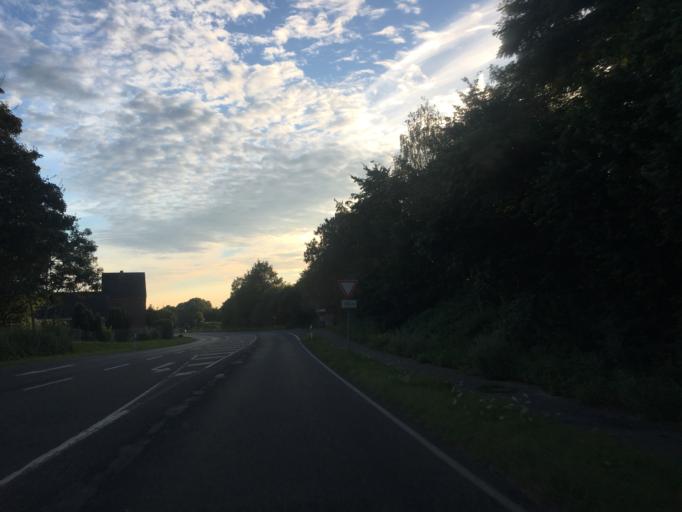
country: DE
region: North Rhine-Westphalia
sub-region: Regierungsbezirk Koln
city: Linnich
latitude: 50.9850
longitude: 6.3024
